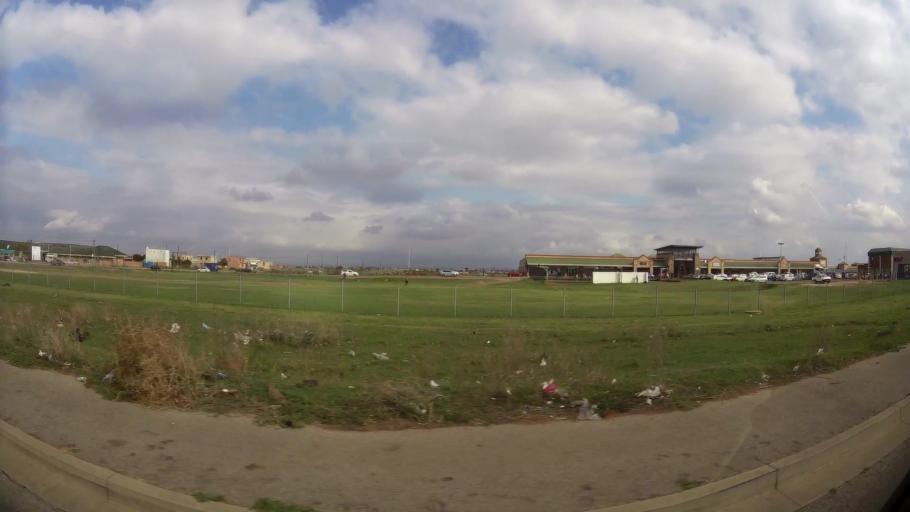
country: ZA
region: Eastern Cape
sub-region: Nelson Mandela Bay Metropolitan Municipality
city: Port Elizabeth
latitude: -33.8104
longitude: 25.5970
